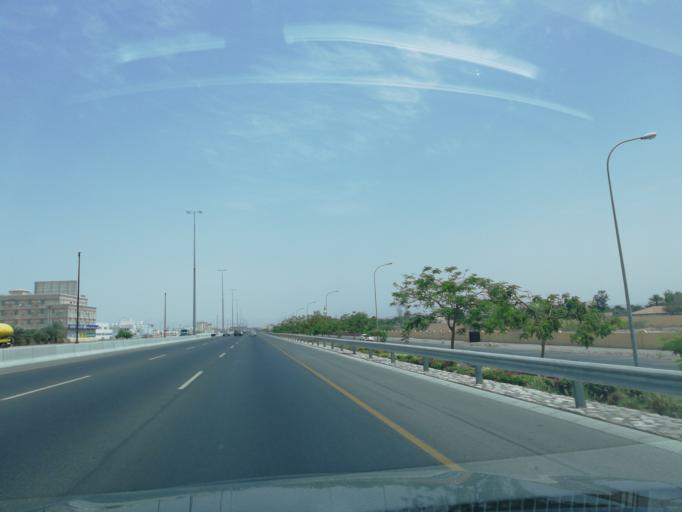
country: OM
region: Muhafazat Masqat
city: As Sib al Jadidah
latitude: 23.6380
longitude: 58.2266
